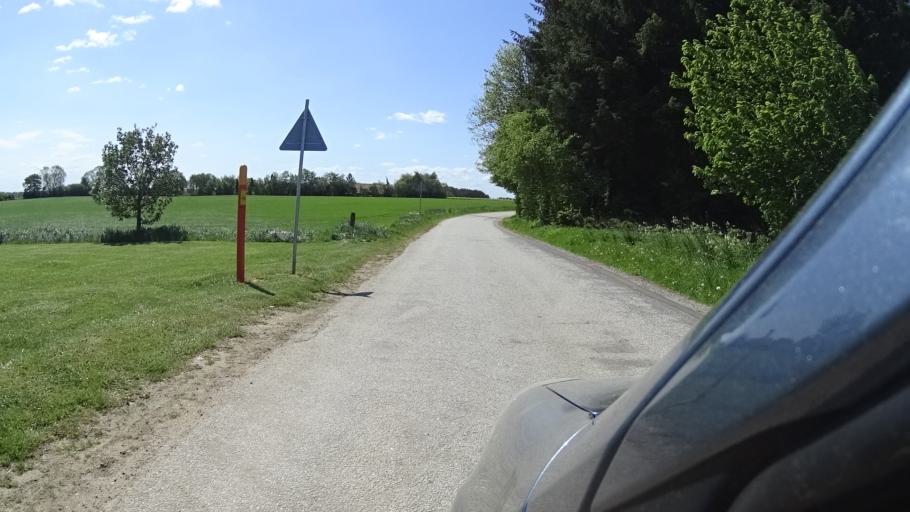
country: DK
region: South Denmark
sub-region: Vejle Kommune
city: Borkop
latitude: 55.6286
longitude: 9.6484
